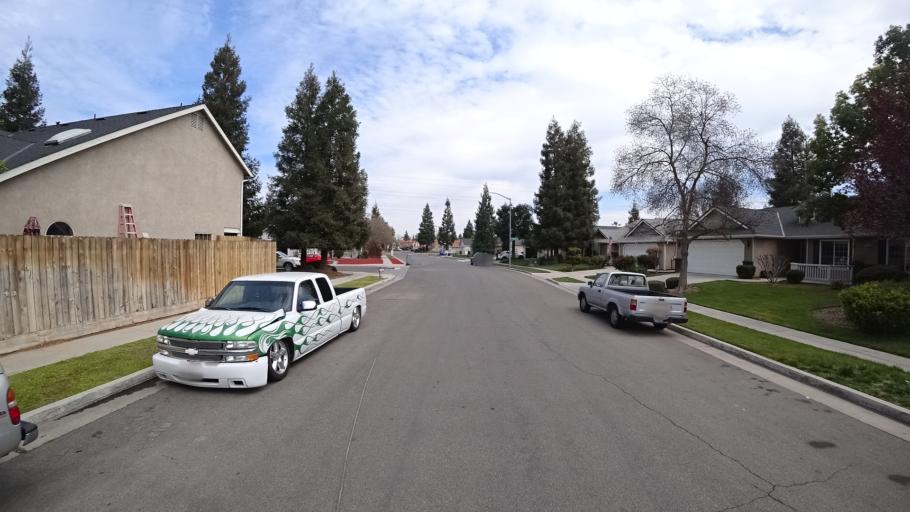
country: US
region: California
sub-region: Fresno County
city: Biola
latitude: 36.8328
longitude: -119.8968
